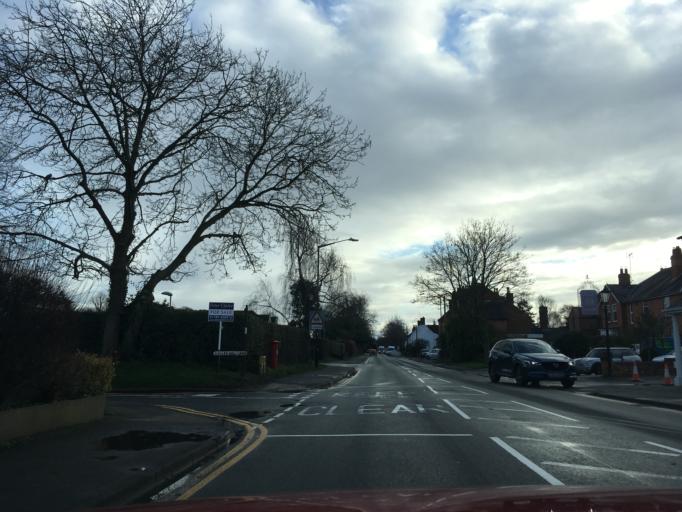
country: GB
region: England
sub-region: Warwickshire
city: Alcester
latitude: 52.2196
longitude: -1.8767
